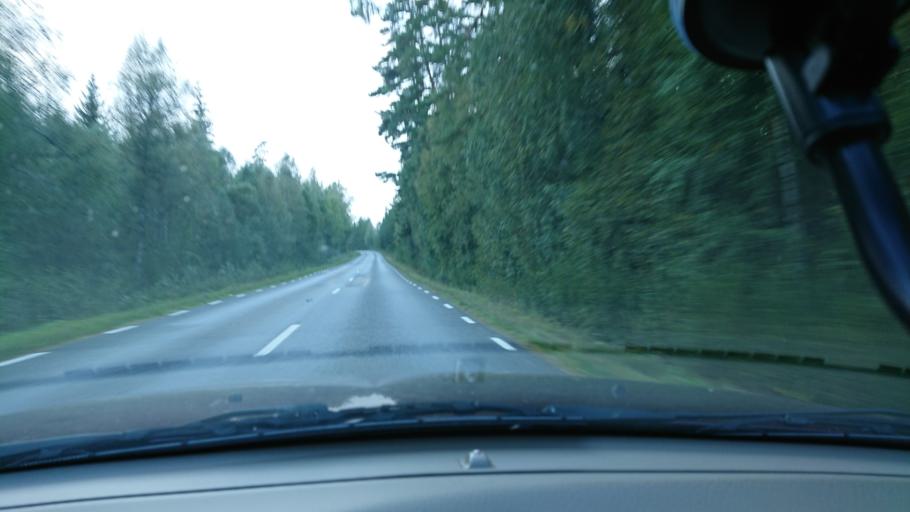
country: SE
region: Kronoberg
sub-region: Vaxjo Kommun
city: Rottne
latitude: 57.0670
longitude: 14.7392
